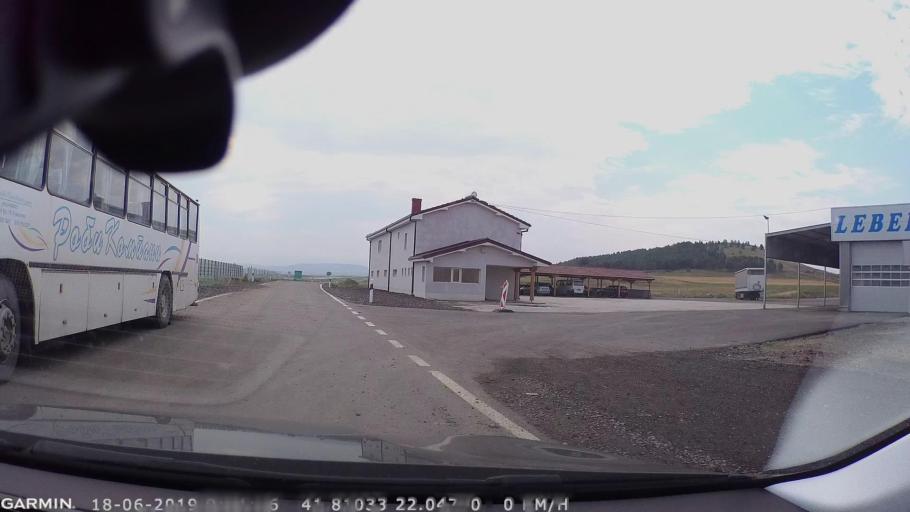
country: MK
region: Sveti Nikole
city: Sveti Nikole
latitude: 41.8044
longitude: 22.0174
